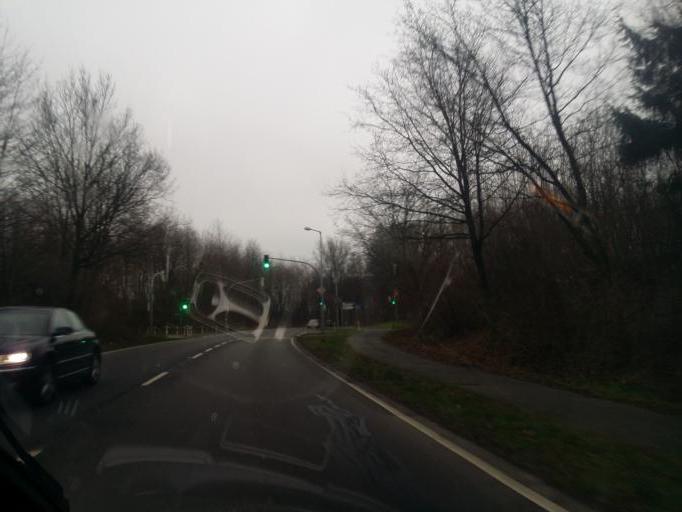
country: DE
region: Schleswig-Holstein
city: Heide
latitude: 54.2023
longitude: 9.1219
